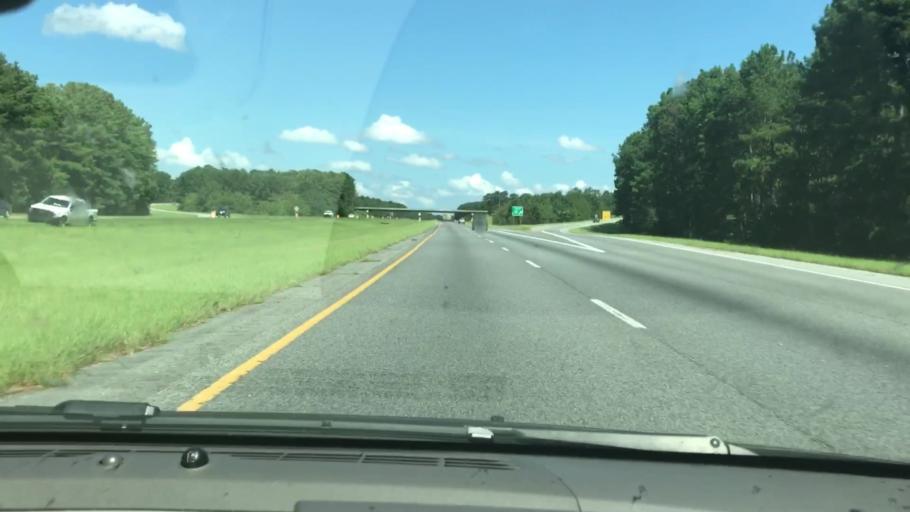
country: US
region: Georgia
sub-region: Harris County
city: Hamilton
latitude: 32.6584
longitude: -84.9769
